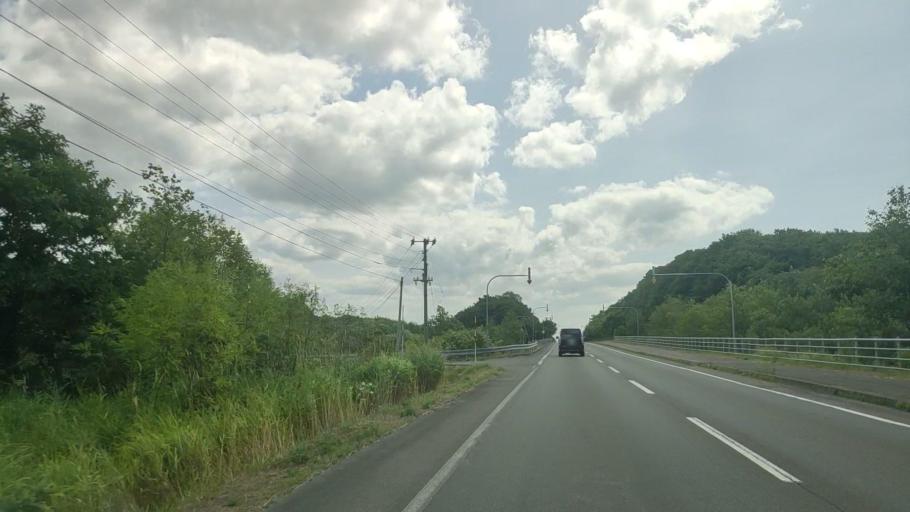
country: JP
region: Hokkaido
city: Makubetsu
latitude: 44.7661
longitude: 141.7932
